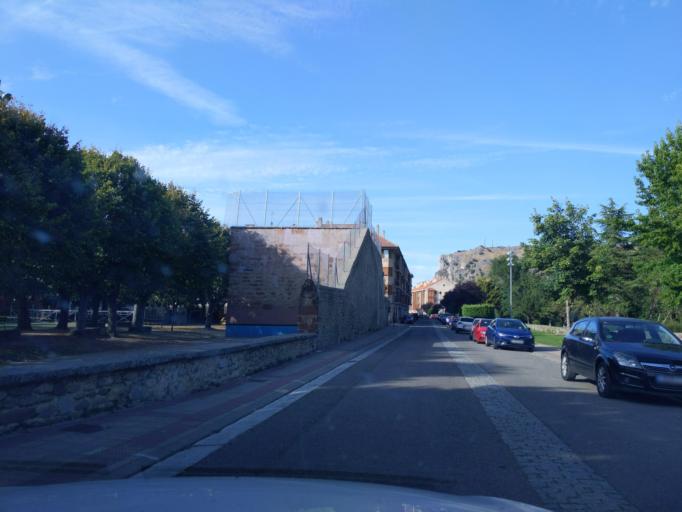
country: ES
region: La Rioja
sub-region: Provincia de La Rioja
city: Ezcaray
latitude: 42.3216
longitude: -3.0132
